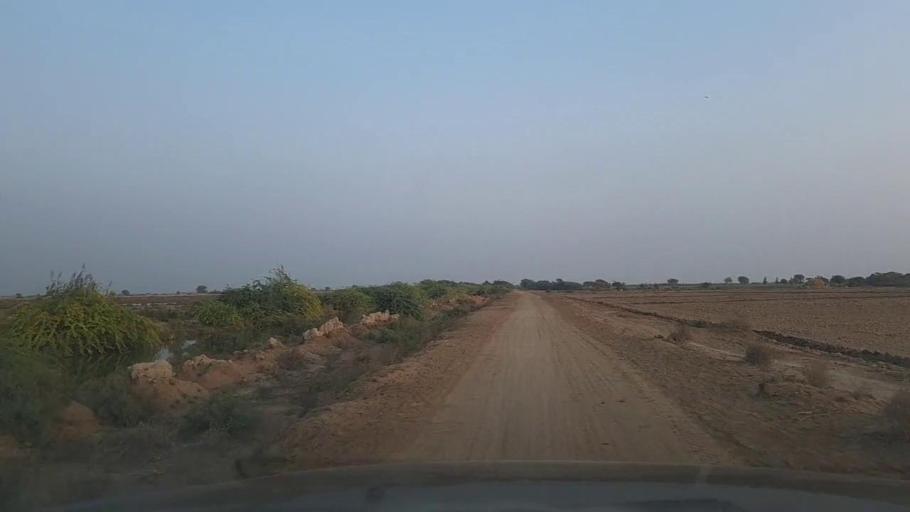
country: PK
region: Sindh
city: Jati
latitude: 24.5406
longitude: 68.4000
